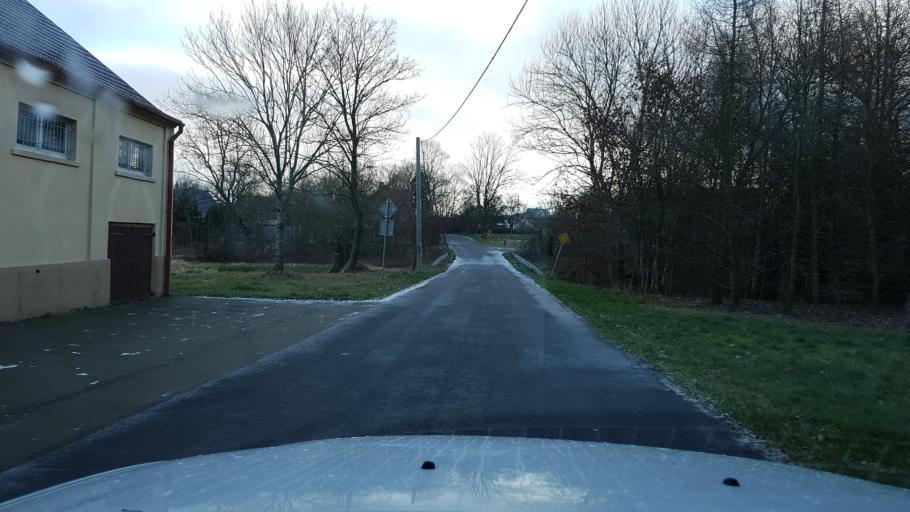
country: PL
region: West Pomeranian Voivodeship
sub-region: Powiat gryficki
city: Brojce
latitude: 54.0329
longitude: 15.3626
